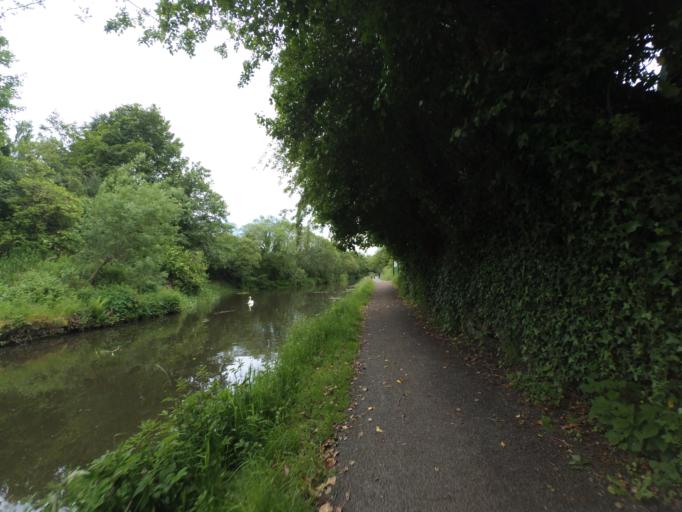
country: GB
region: Scotland
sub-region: Falkirk
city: Polmont
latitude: 55.9826
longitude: -3.7153
